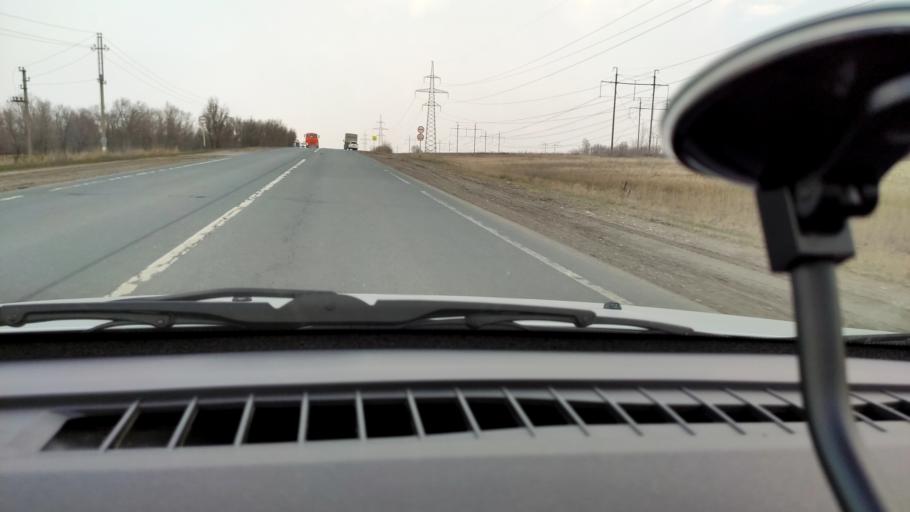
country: RU
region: Samara
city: Dubovyy Umet
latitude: 53.0684
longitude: 50.3807
